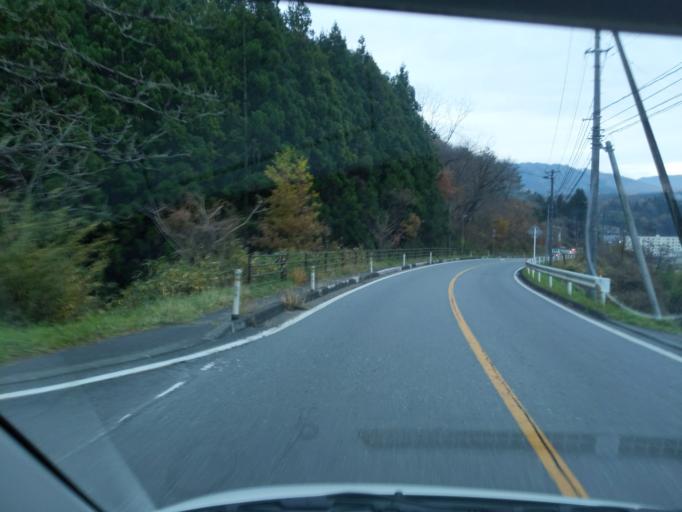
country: JP
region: Iwate
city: Ichinoseki
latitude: 38.9994
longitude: 141.3235
